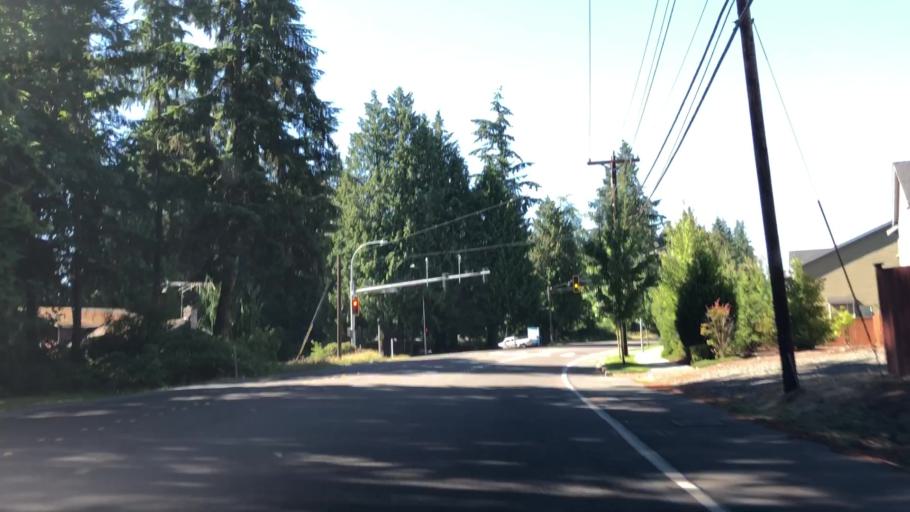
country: US
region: Washington
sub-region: Snohomish County
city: North Creek
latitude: 47.8170
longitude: -122.1859
